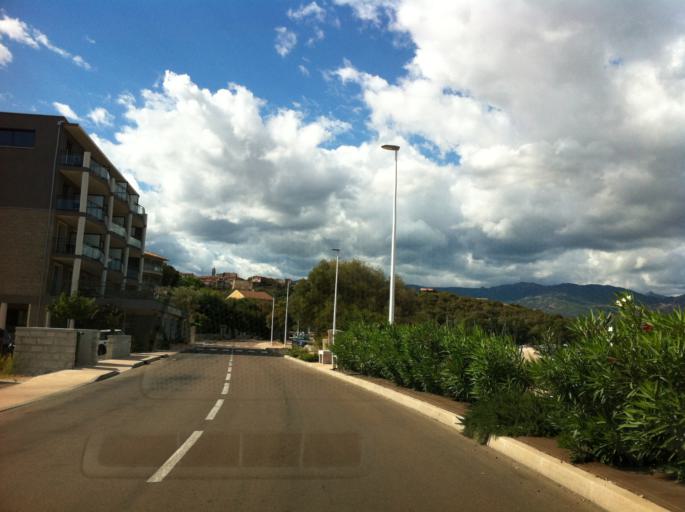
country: FR
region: Corsica
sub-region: Departement de la Corse-du-Sud
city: Porto-Vecchio
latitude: 41.5883
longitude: 9.2879
